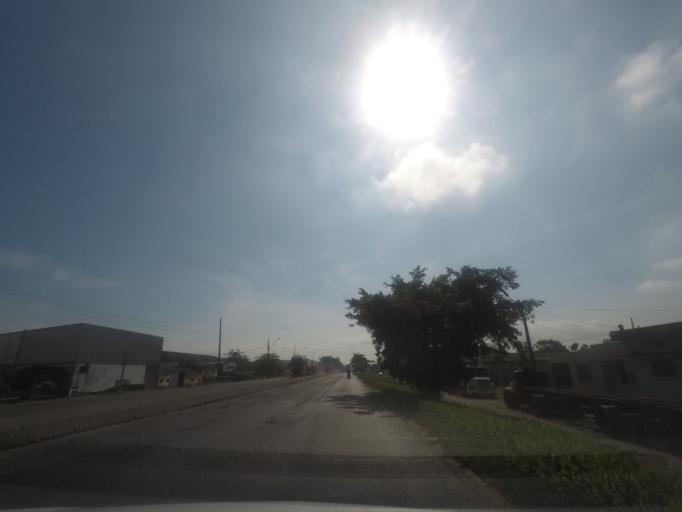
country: BR
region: Parana
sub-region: Paranagua
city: Paranagua
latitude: -25.5191
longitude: -48.5245
